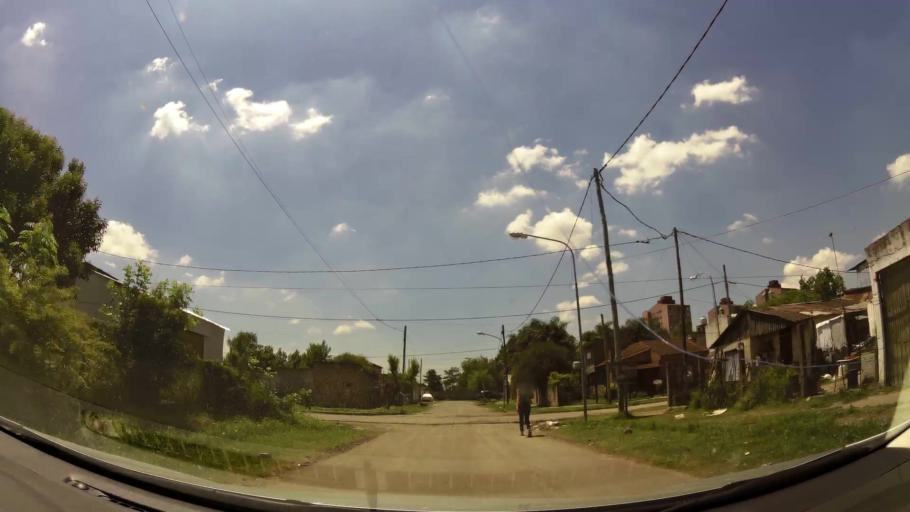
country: AR
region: Buenos Aires
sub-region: Partido de Tigre
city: Tigre
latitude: -34.4402
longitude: -58.5890
